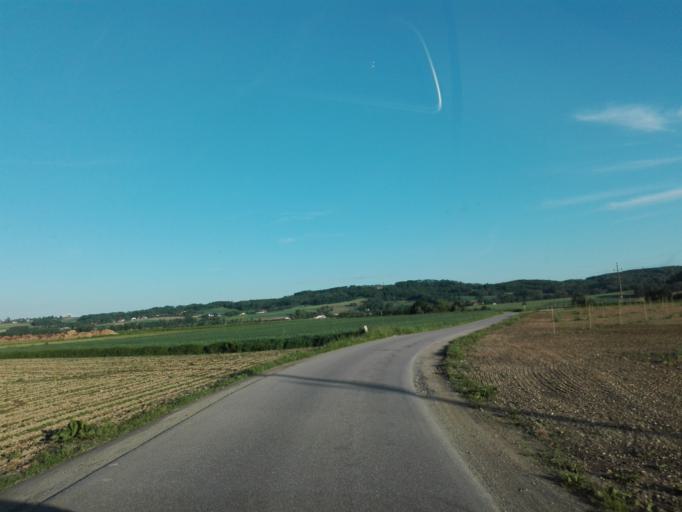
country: AT
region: Upper Austria
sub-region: Politischer Bezirk Urfahr-Umgebung
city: Goldworth
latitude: 48.2820
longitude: 14.0771
